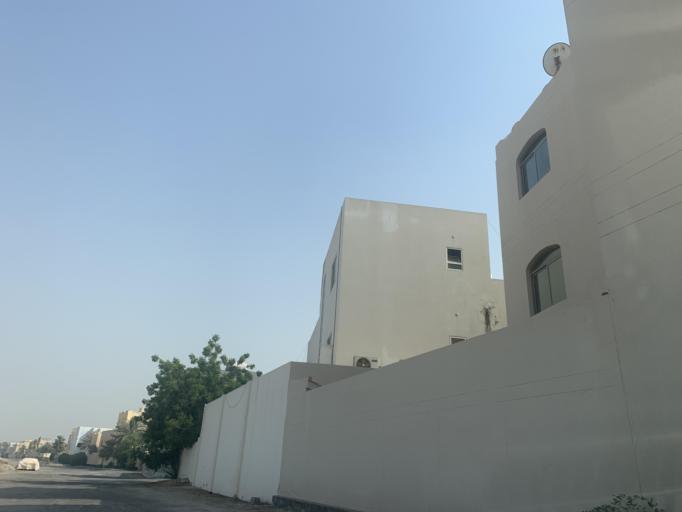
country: BH
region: Manama
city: Jidd Hafs
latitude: 26.2082
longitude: 50.4937
